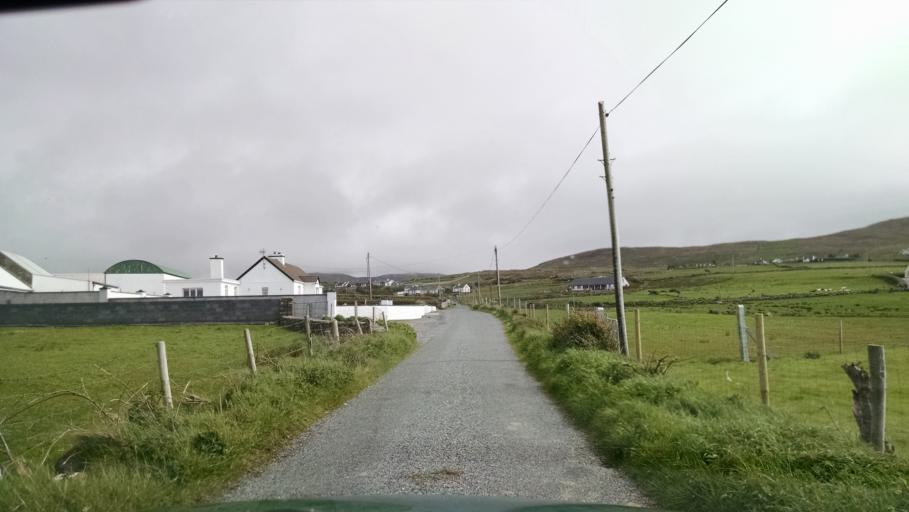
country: IE
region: Connaught
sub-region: County Galway
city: Clifden
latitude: 53.7143
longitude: -9.8865
